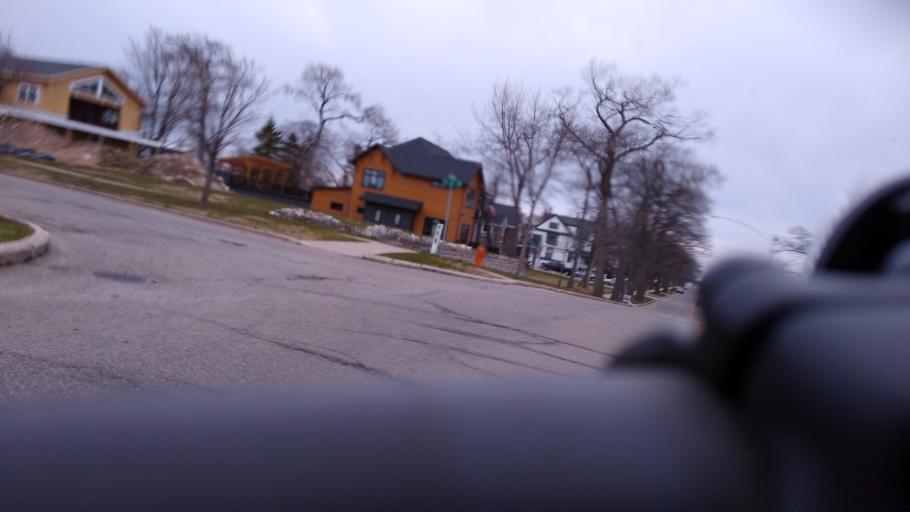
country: US
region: Michigan
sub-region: Delta County
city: Escanaba
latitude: 45.7411
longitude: -87.0528
